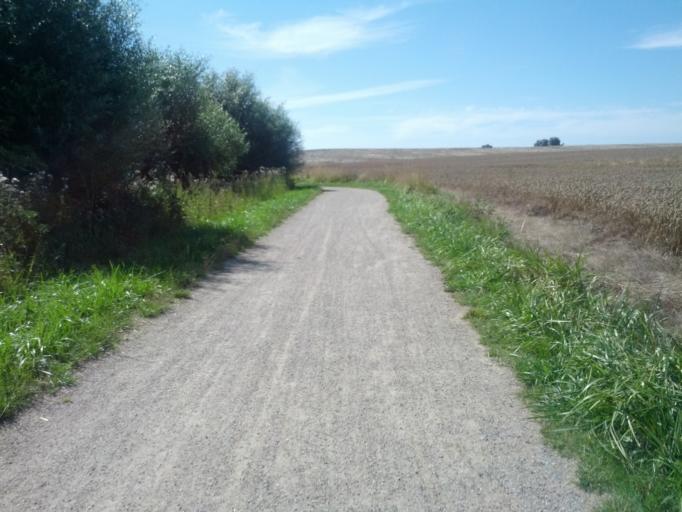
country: DE
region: Mecklenburg-Vorpommern
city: Bastorf
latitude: 54.1404
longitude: 11.6933
